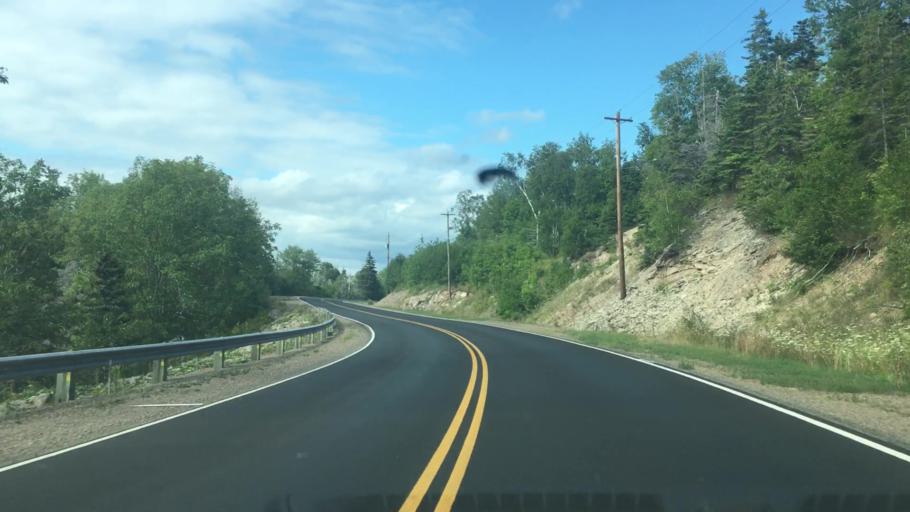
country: CA
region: Nova Scotia
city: Princeville
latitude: 45.7929
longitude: -60.7371
